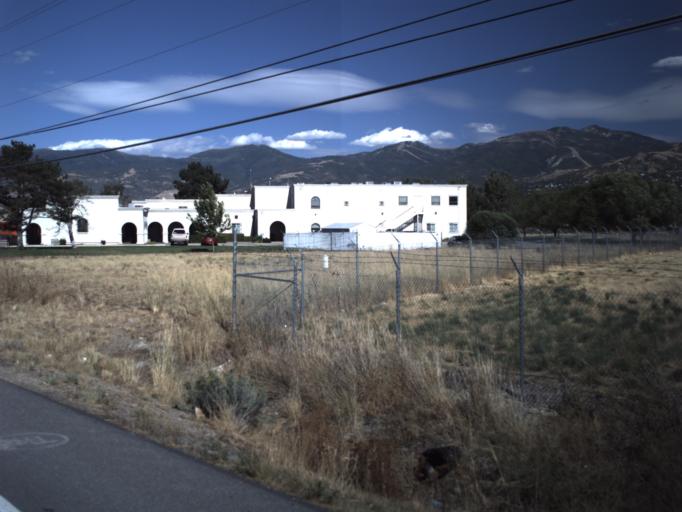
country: US
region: Utah
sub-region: Davis County
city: North Salt Lake
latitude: 40.8406
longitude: -111.9324
